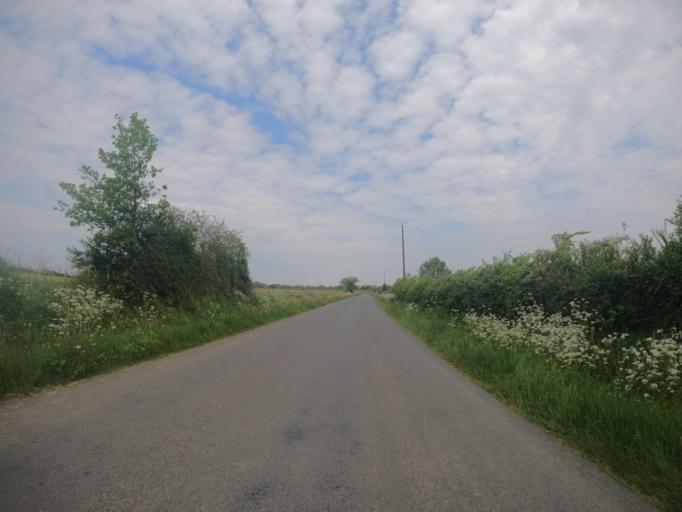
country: FR
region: Poitou-Charentes
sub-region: Departement des Deux-Sevres
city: Saint-Varent
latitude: 46.8718
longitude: -0.2935
